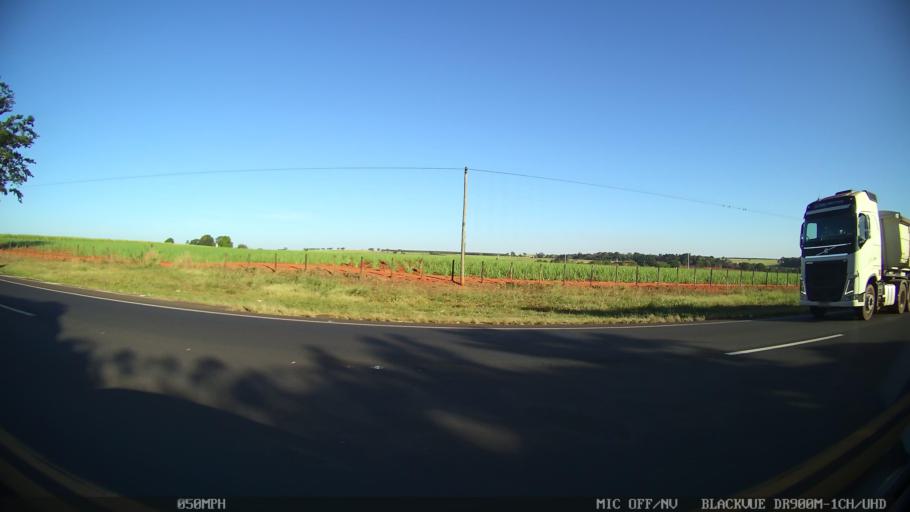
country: BR
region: Sao Paulo
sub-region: Guapiacu
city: Guapiacu
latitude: -20.7545
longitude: -49.1511
